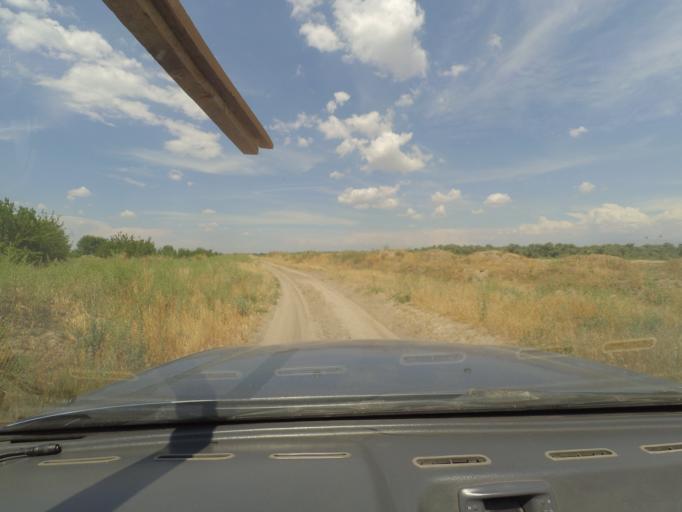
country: TJ
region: Viloyati Sughd
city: Buston
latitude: 40.5385
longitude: 69.0787
